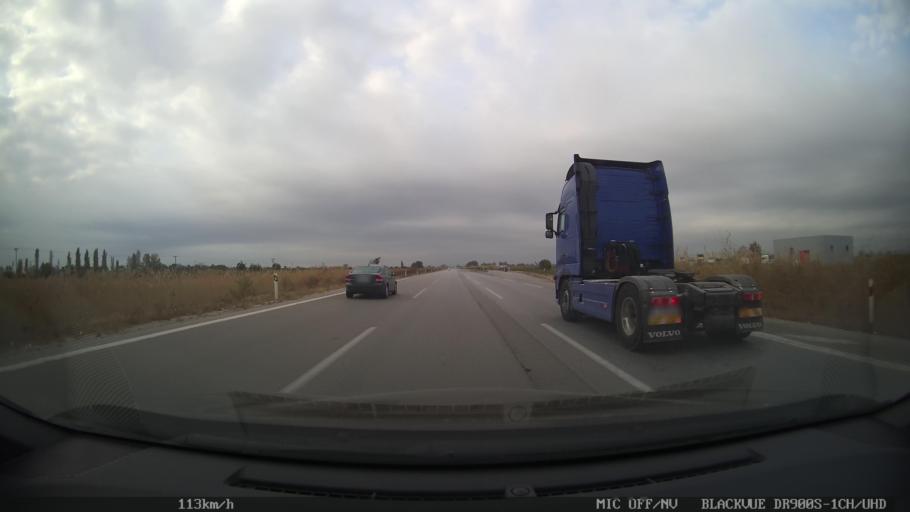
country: GR
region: Central Macedonia
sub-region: Nomos Thessalonikis
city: Chalastra
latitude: 40.6269
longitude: 22.7676
